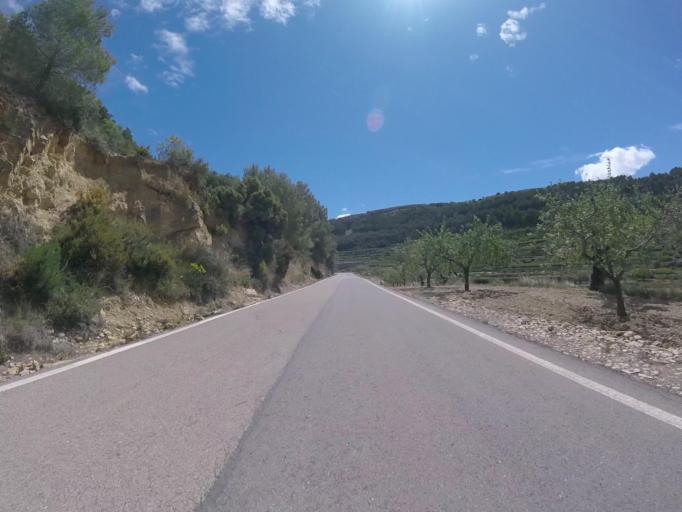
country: ES
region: Valencia
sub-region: Provincia de Castello
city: Sierra-Engarceran
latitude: 40.2726
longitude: -0.0163
